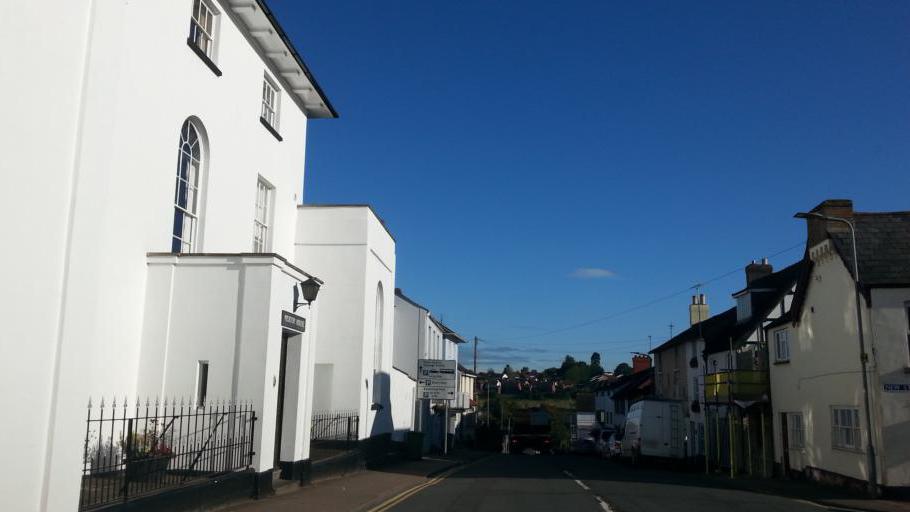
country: GB
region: England
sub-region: Herefordshire
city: Ross on Wye
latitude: 51.9155
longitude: -2.5858
